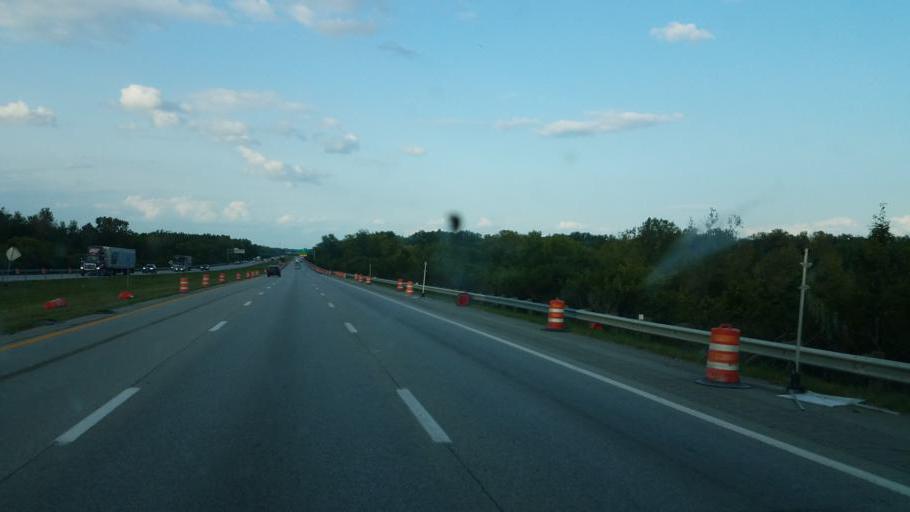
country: US
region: Ohio
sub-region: Franklin County
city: Obetz
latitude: 39.8824
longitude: -82.9175
